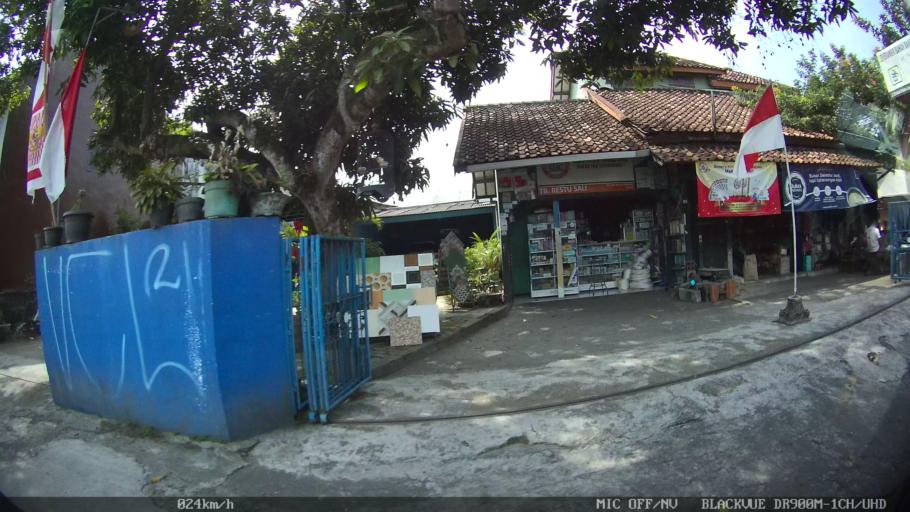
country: ID
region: Daerah Istimewa Yogyakarta
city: Depok
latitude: -7.8029
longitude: 110.4212
